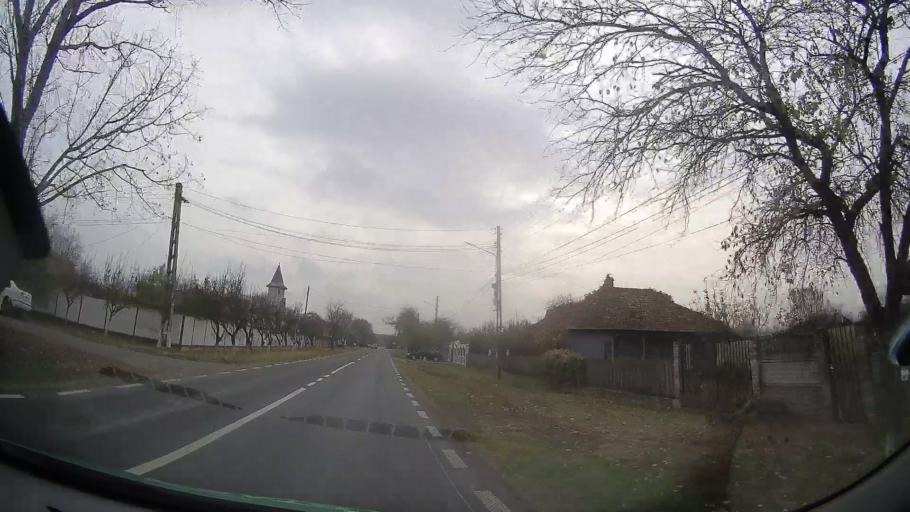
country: RO
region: Ilfov
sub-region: Comuna Gruiu
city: Lipia
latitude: 44.7162
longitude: 26.2737
